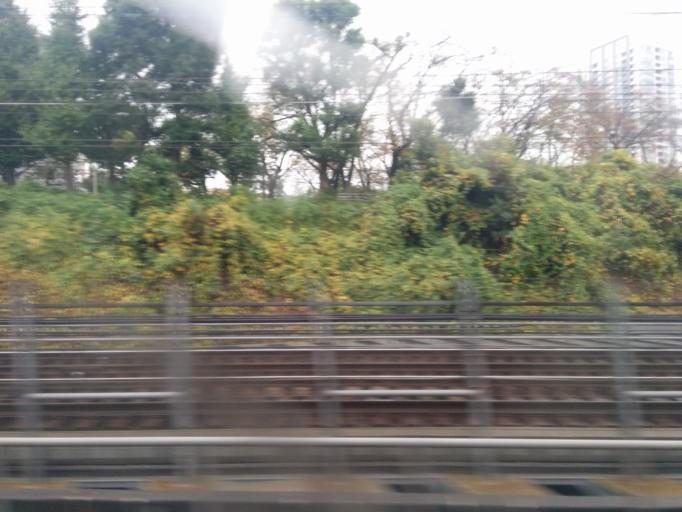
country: JP
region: Tokyo
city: Tokyo
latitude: 35.6190
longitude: 139.7372
